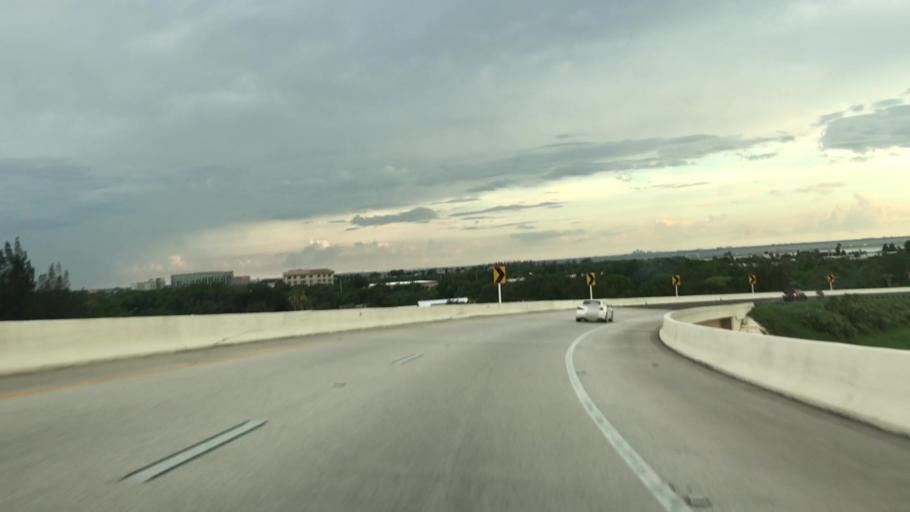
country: US
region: Florida
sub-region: Hillsborough County
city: Town 'n' Country
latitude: 27.9565
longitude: -82.5390
